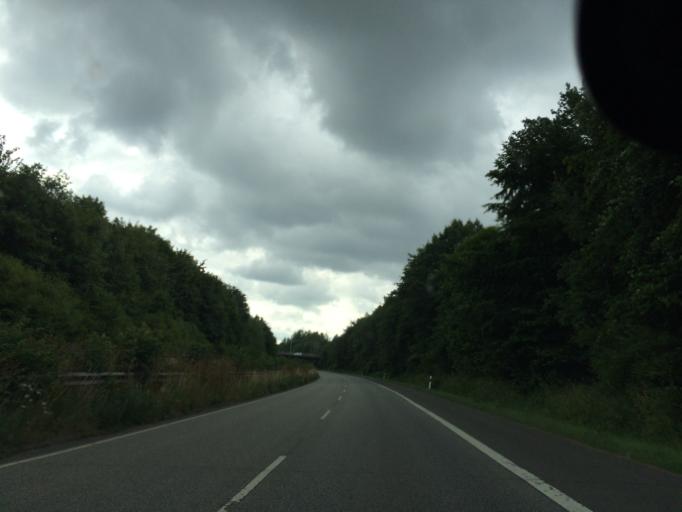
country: DE
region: Schleswig-Holstein
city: Kronshagen
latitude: 54.3539
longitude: 10.1000
